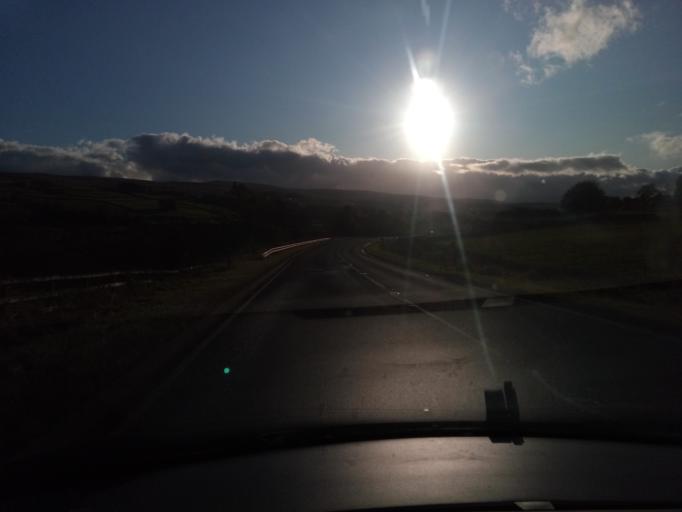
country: GB
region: England
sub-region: County Durham
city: Stanhope
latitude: 54.7483
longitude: -2.0296
